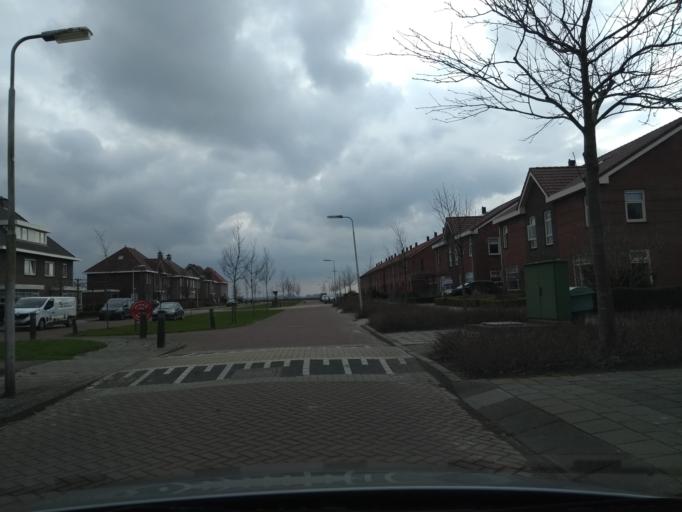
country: NL
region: Flevoland
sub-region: Gemeente Noordoostpolder
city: Ens
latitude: 52.7408
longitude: 5.8528
